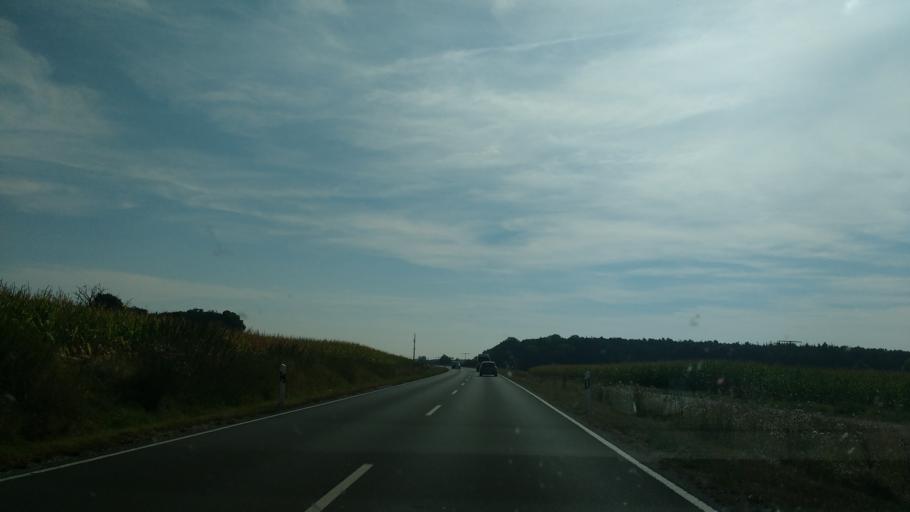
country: DE
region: Bavaria
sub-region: Regierungsbezirk Mittelfranken
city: Grossenseebach
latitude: 49.6325
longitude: 10.8874
